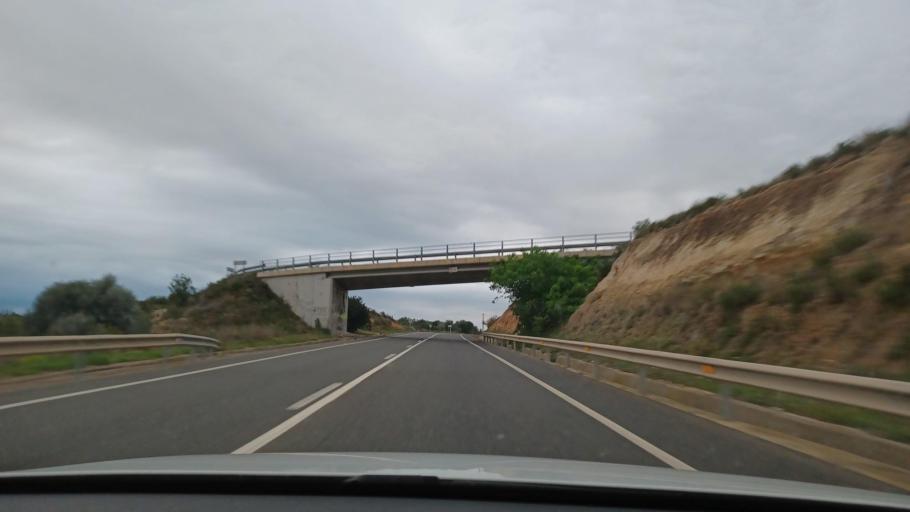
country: ES
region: Catalonia
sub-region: Provincia de Tarragona
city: Amposta
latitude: 40.7149
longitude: 0.5640
